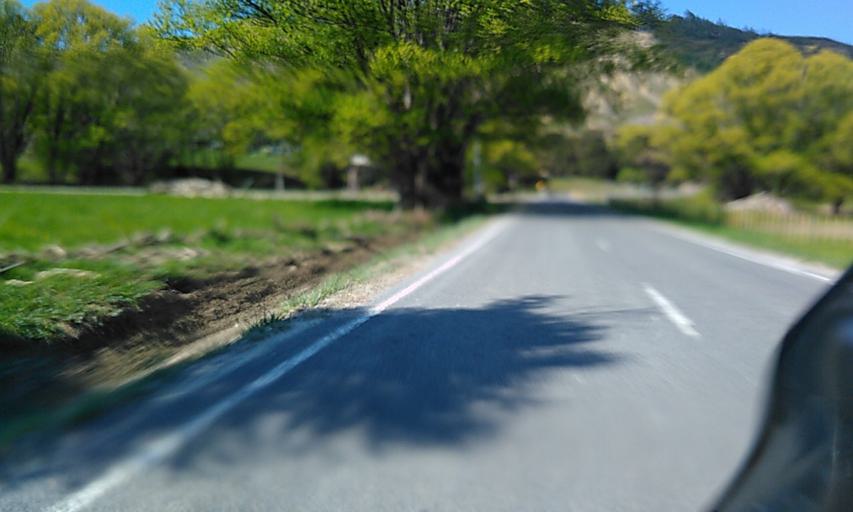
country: NZ
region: Gisborne
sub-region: Gisborne District
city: Gisborne
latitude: -38.3256
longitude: 178.1935
